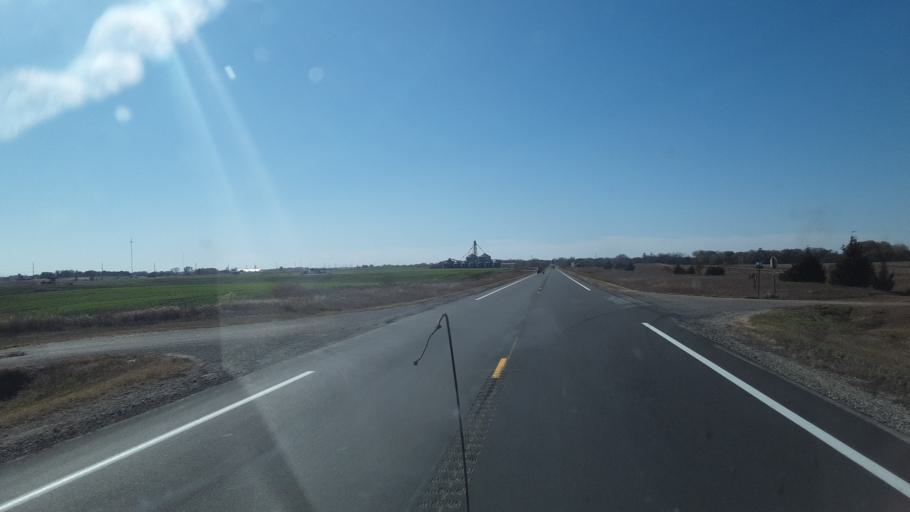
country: US
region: Kansas
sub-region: Rice County
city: Lyons
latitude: 38.3624
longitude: -98.1669
